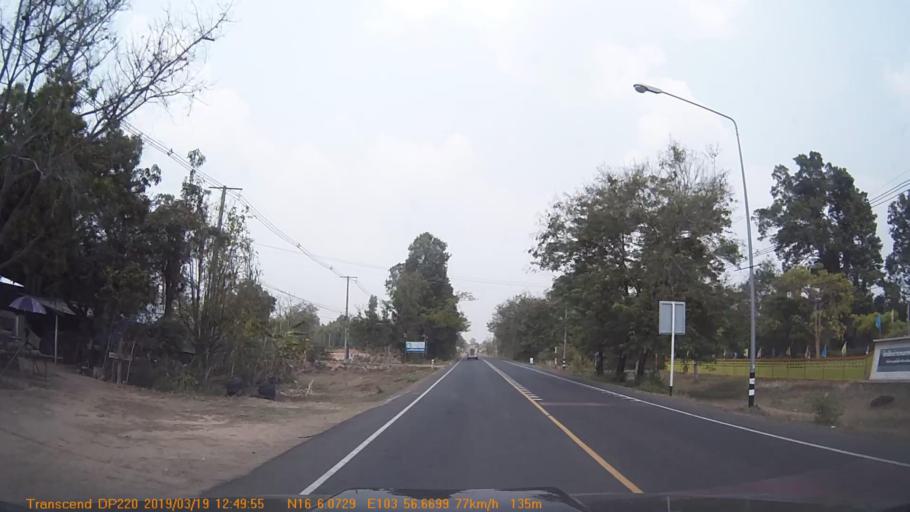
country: TH
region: Roi Et
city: Selaphum
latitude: 16.1016
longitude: 103.9445
